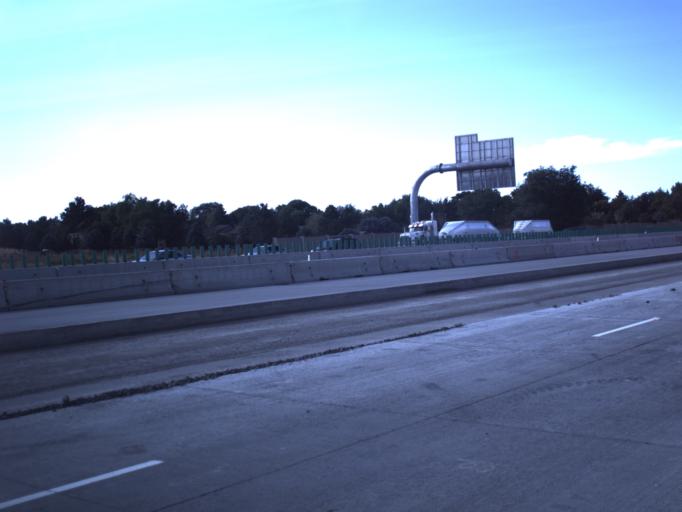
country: US
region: Utah
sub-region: Salt Lake County
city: Taylorsville
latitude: 40.6778
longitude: -111.9519
